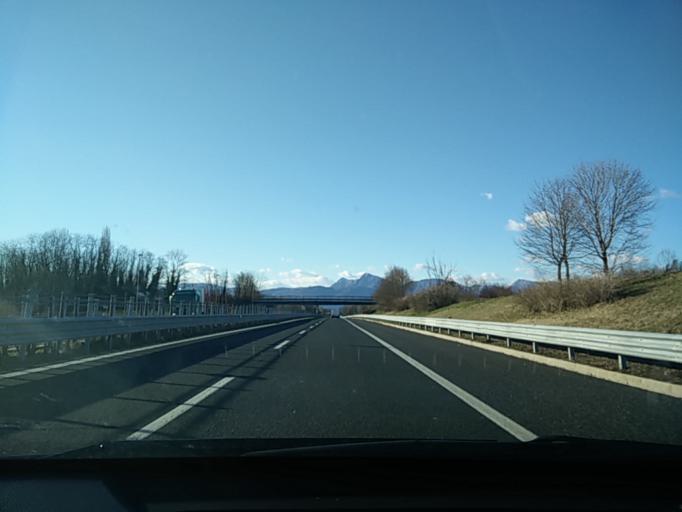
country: IT
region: Friuli Venezia Giulia
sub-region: Provincia di Udine
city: Collofedo di Monte Albano
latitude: 46.1690
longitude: 13.1527
